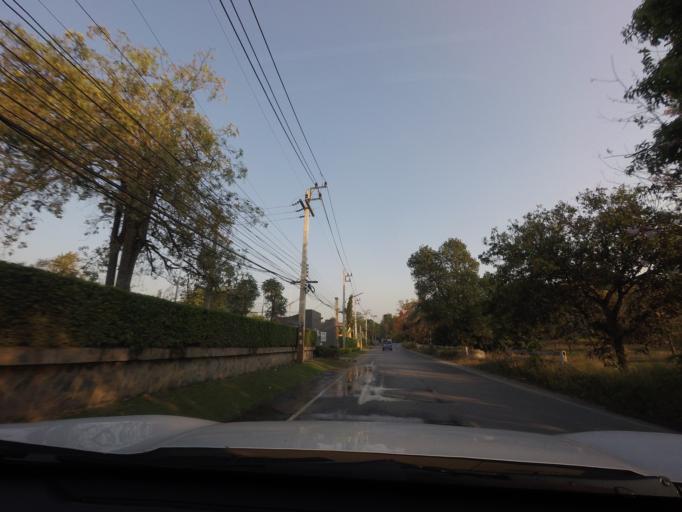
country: TH
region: Nakhon Ratchasima
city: Pak Chong
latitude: 14.6407
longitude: 101.4197
